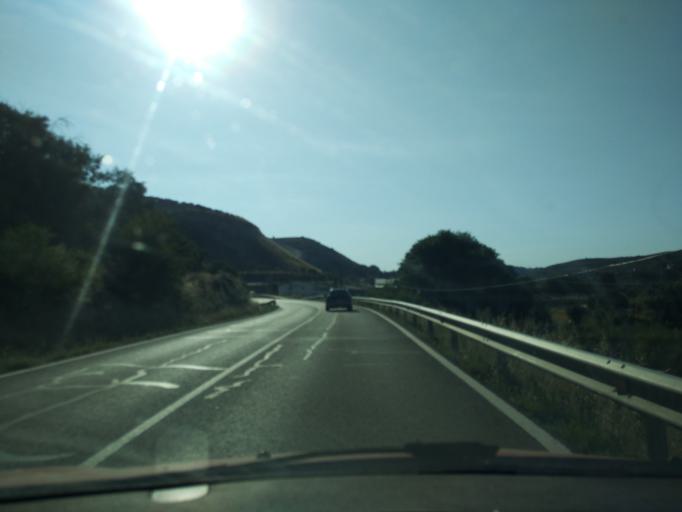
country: ES
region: Madrid
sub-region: Provincia de Madrid
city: Valverde de Alcala
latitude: 40.4176
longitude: -3.3087
